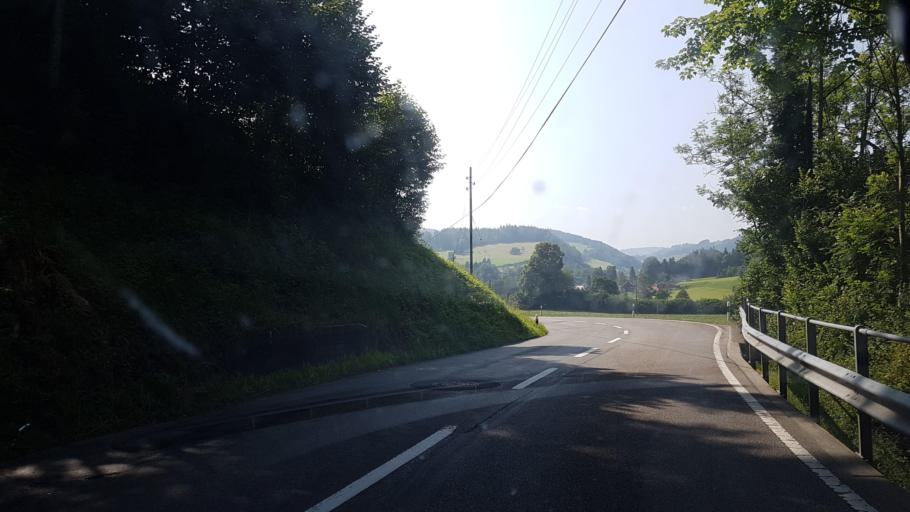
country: CH
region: Saint Gallen
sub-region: Wahlkreis Toggenburg
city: Mogelsberg
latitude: 47.3637
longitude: 9.1257
